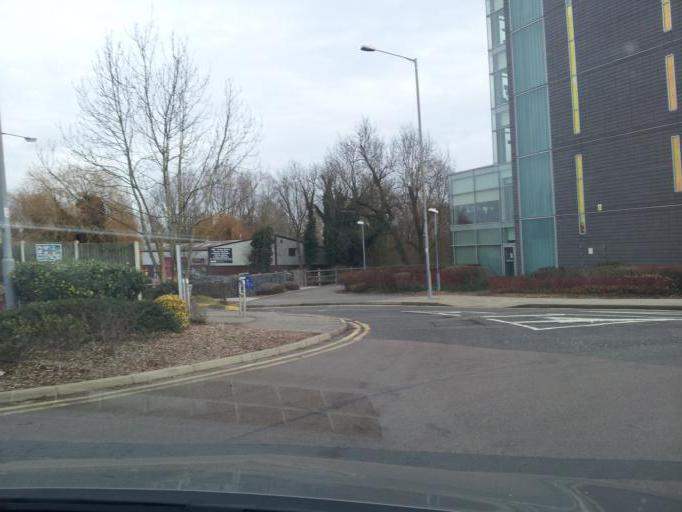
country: GB
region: England
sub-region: Essex
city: Chelmsford
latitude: 51.7418
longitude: 0.4731
